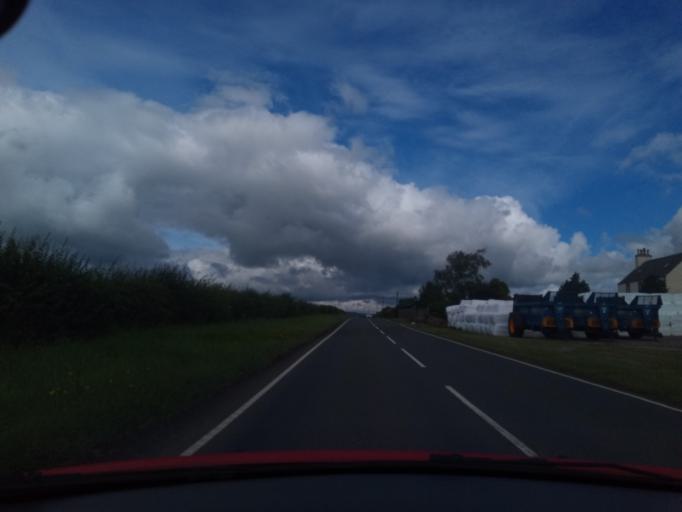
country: GB
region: Scotland
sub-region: The Scottish Borders
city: Lauder
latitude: 55.7389
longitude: -2.7424
